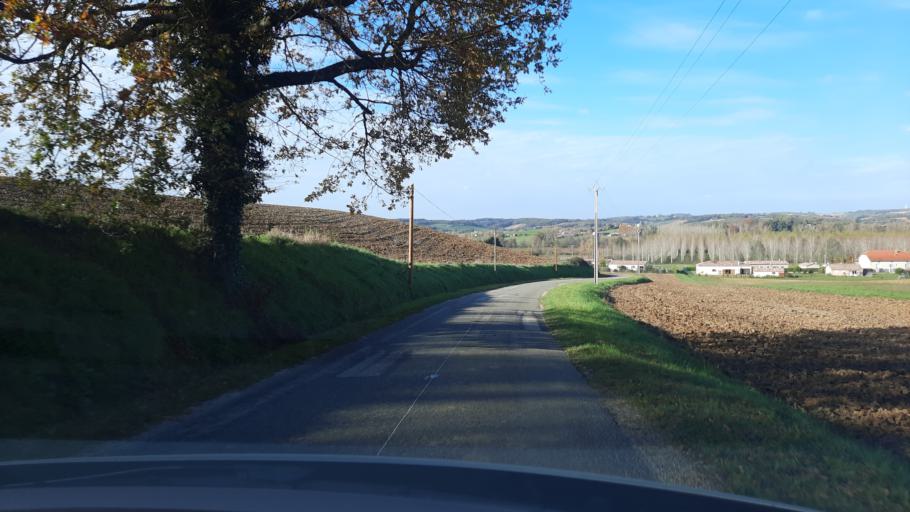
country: FR
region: Midi-Pyrenees
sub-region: Departement du Tarn-et-Garonne
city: Lafrancaise
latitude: 44.1542
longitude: 1.2748
